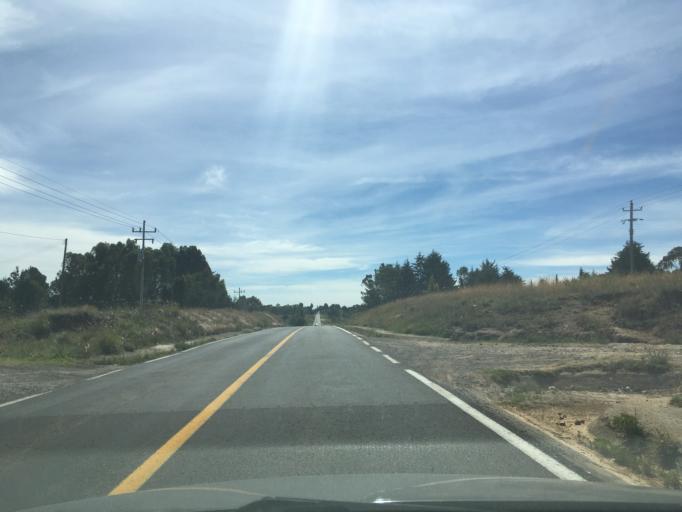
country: MX
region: Queretaro
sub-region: Amealco de Bonfil
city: La Soledad
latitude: 20.1793
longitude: -100.1834
